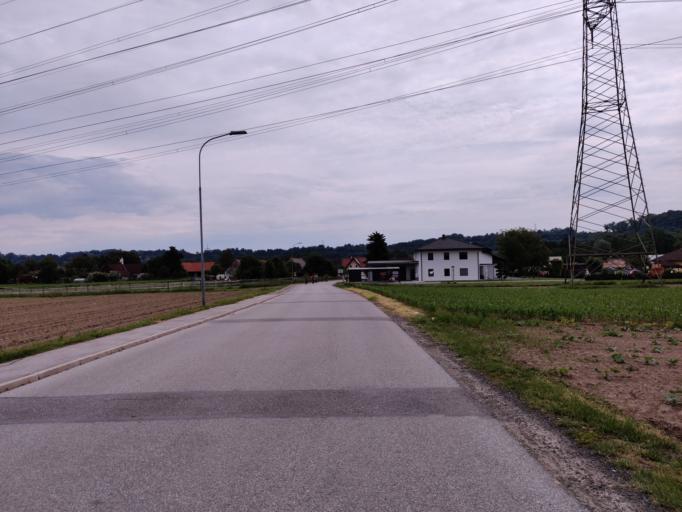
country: AT
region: Styria
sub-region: Politischer Bezirk Graz-Umgebung
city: Werndorf
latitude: 46.9223
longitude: 15.4865
